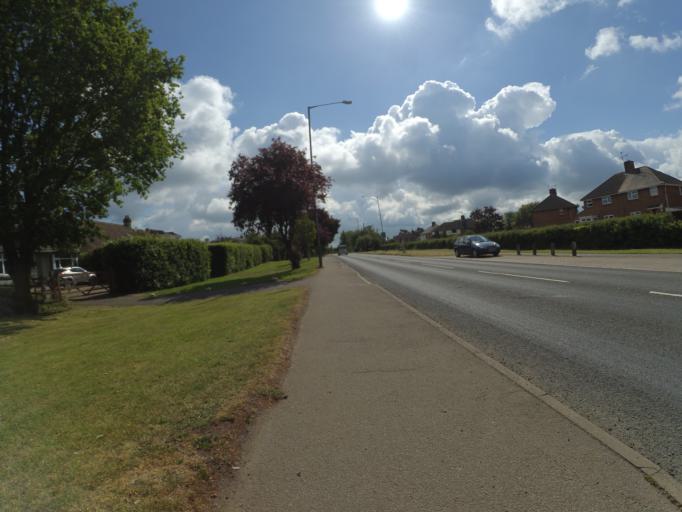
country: GB
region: England
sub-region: Warwickshire
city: Rugby
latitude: 52.3579
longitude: -1.2124
